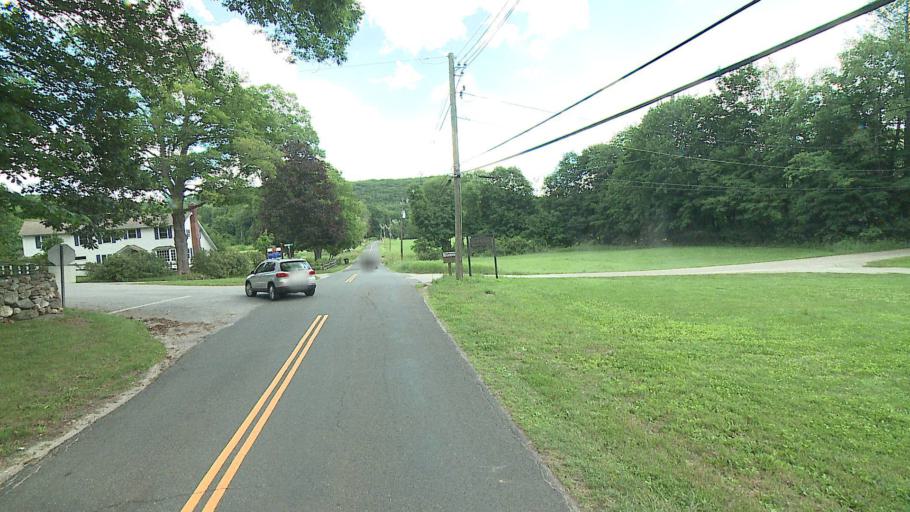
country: US
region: Connecticut
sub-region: Litchfield County
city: New Preston
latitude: 41.7030
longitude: -73.3511
